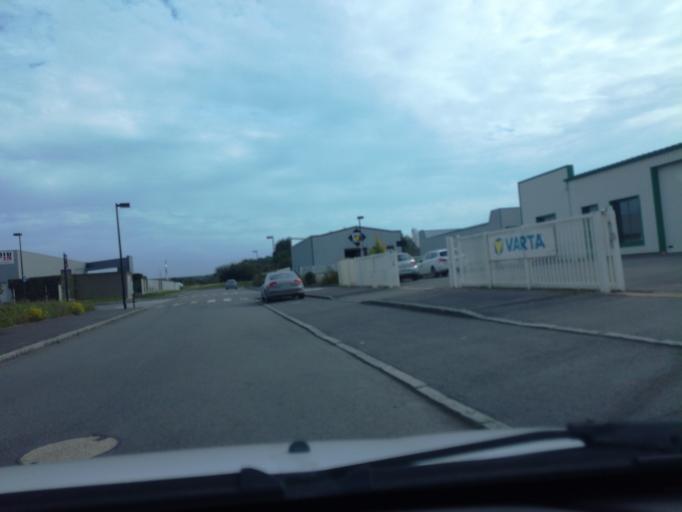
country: FR
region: Brittany
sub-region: Departement d'Ille-et-Vilaine
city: Saint-Jacques-de-la-Lande
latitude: 48.0662
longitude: -1.7002
